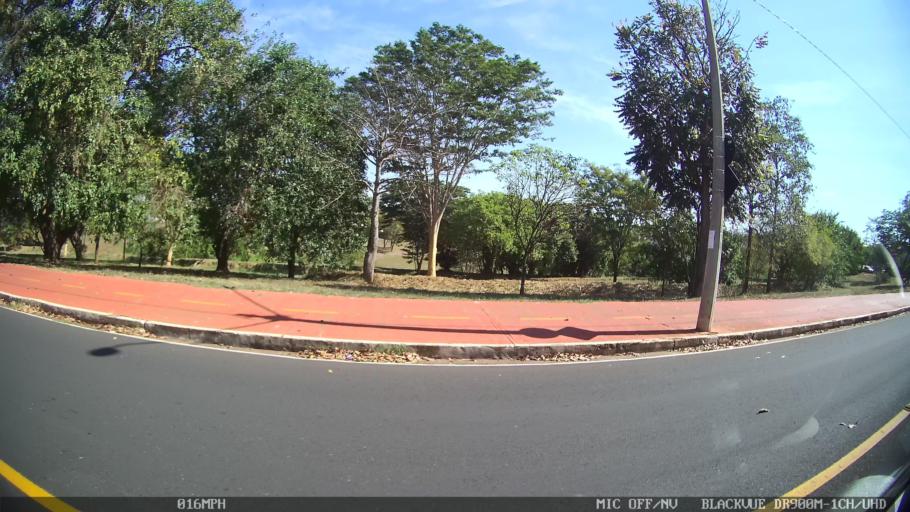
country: BR
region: Sao Paulo
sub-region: Sao Jose Do Rio Preto
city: Sao Jose do Rio Preto
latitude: -20.7838
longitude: -49.4147
